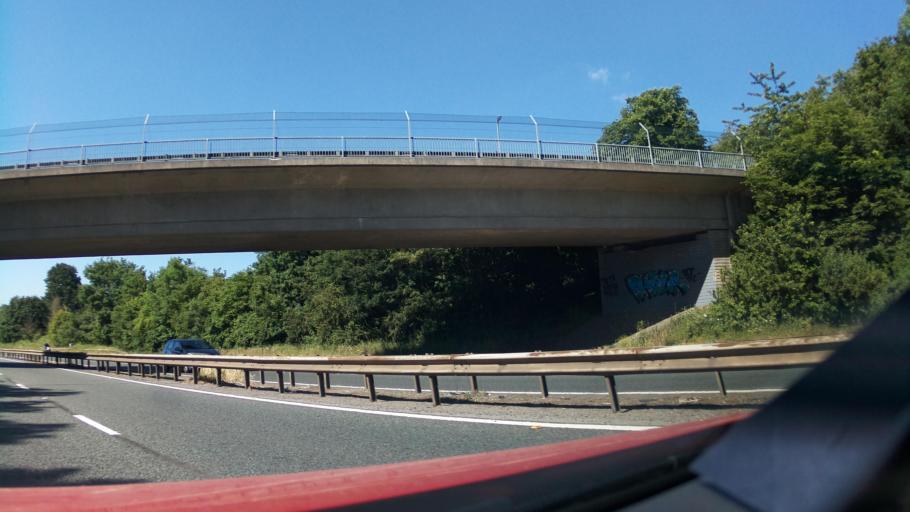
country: GB
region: England
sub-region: South Gloucestershire
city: Stoke Gifford
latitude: 51.4837
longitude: -2.5586
